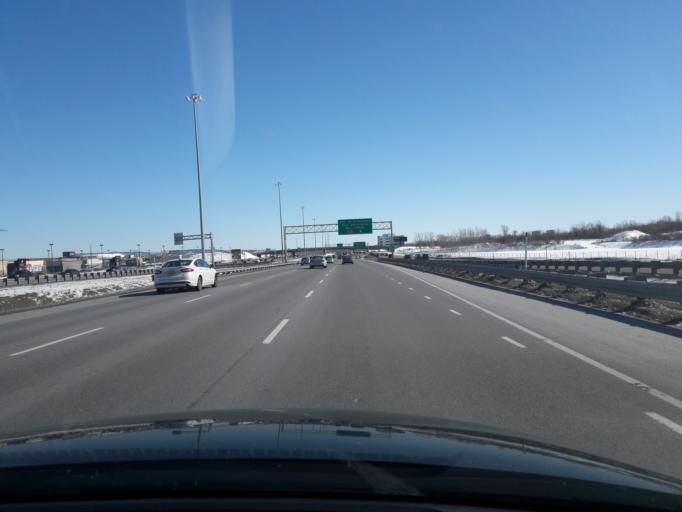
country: CA
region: Quebec
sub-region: Laval
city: Laval
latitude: 45.5623
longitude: -73.7369
